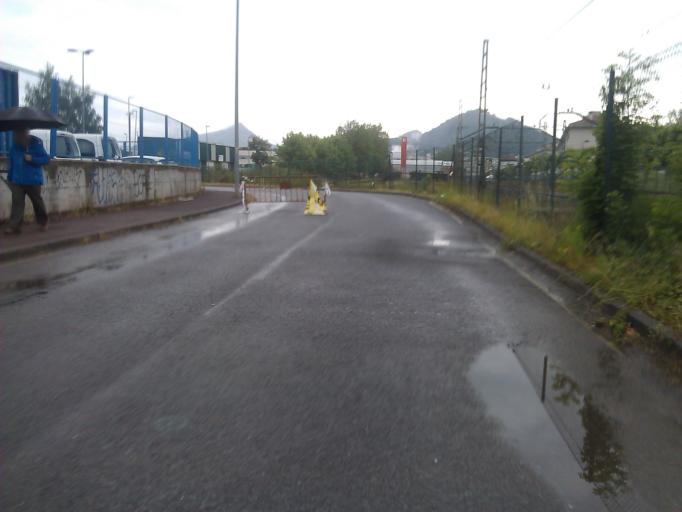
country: ES
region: Basque Country
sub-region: Provincia de Guipuzcoa
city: Astigarraga
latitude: 43.2733
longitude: -1.9606
